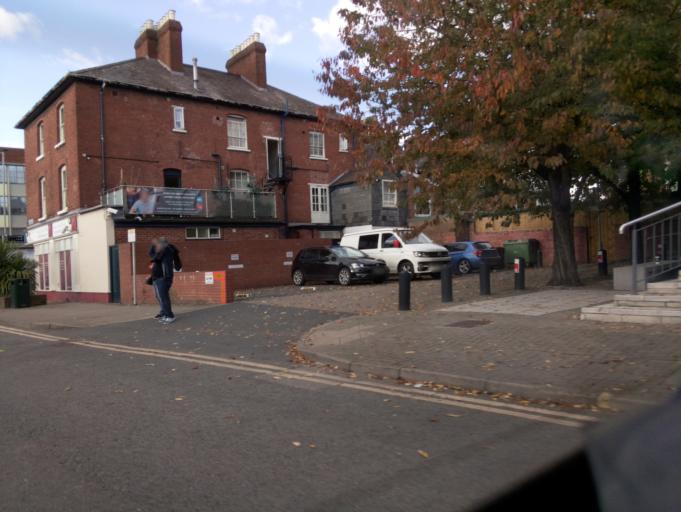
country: GB
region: England
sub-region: Herefordshire
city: Hereford
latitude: 52.0576
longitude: -2.7119
